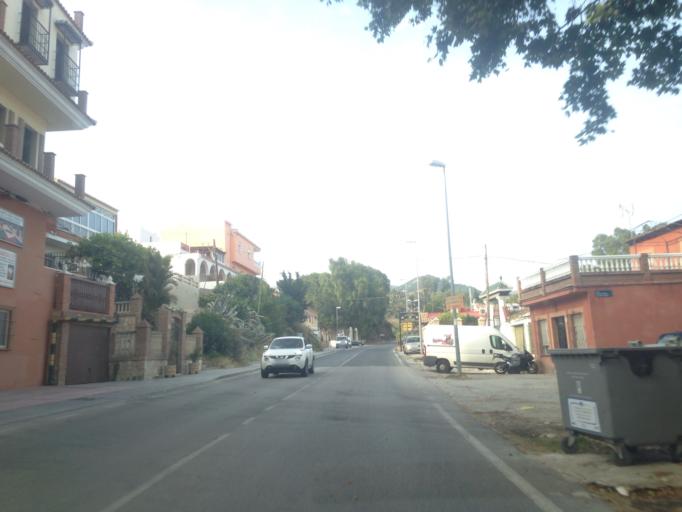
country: ES
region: Andalusia
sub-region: Provincia de Malaga
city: Malaga
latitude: 36.7422
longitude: -4.4118
